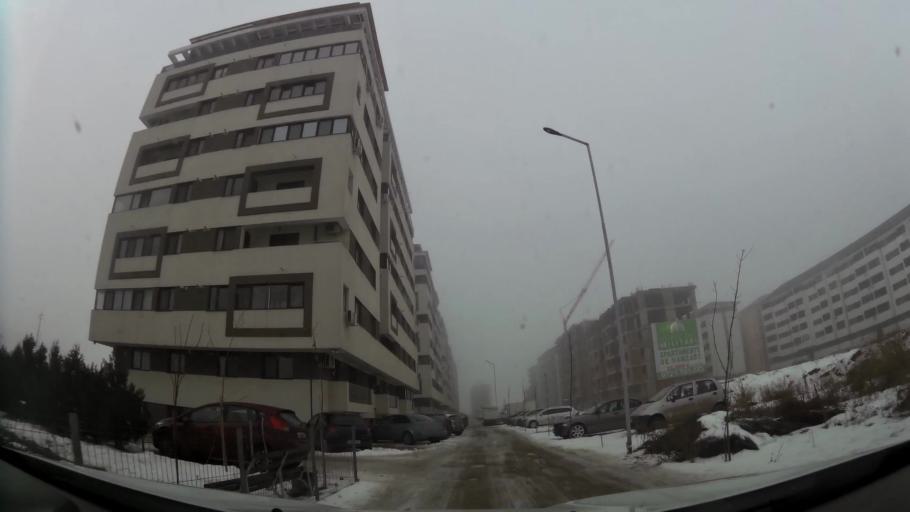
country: RO
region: Ilfov
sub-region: Comuna Chiajna
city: Chiajna
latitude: 44.4462
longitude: 25.9790
